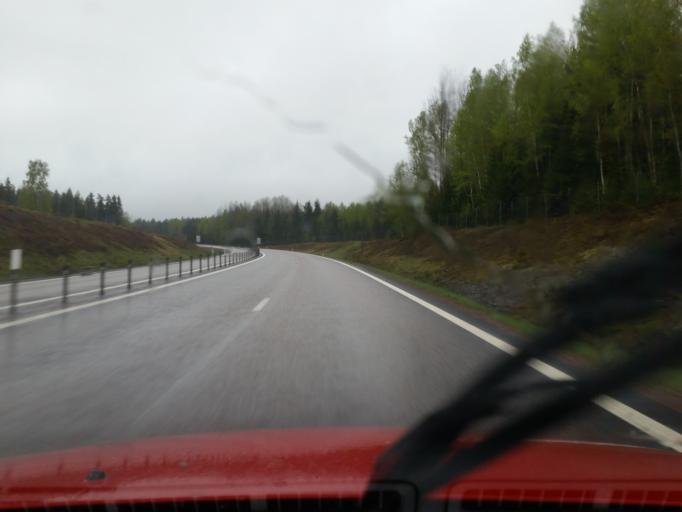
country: SE
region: Dalarna
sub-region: Saters Kommun
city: Saeter
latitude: 60.3945
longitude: 15.6204
